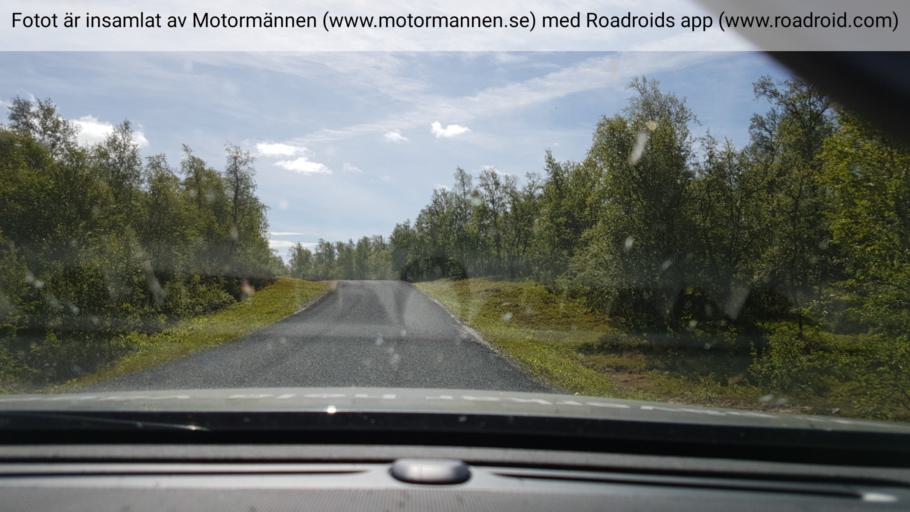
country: NO
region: Nordland
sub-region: Hattfjelldal
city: Hattfjelldal
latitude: 65.4119
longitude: 14.9331
